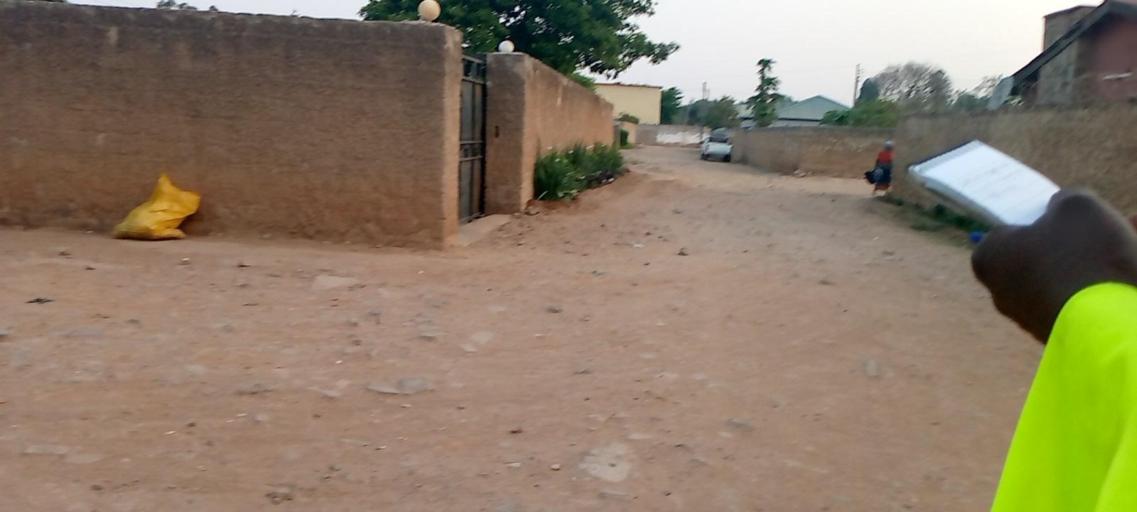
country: ZM
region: Lusaka
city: Lusaka
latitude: -15.4067
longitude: 28.3466
